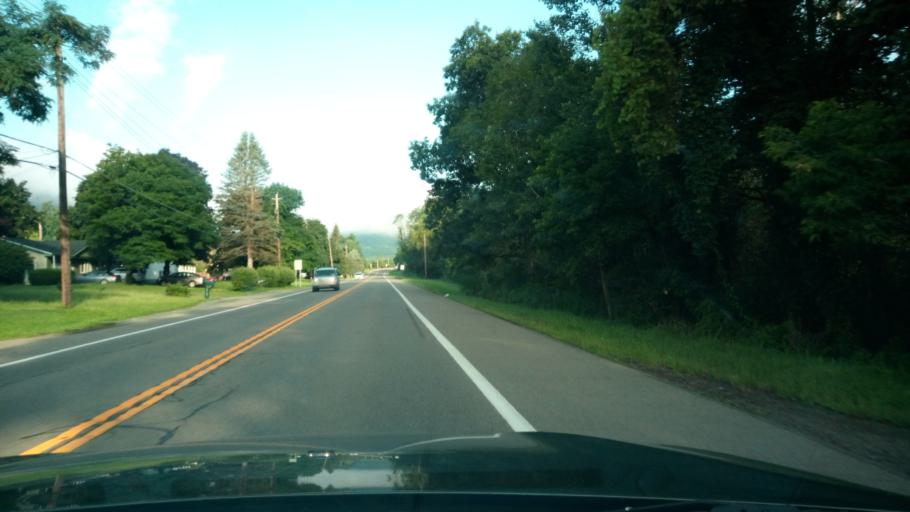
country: US
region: New York
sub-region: Chemung County
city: Big Flats
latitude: 42.0957
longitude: -76.9022
